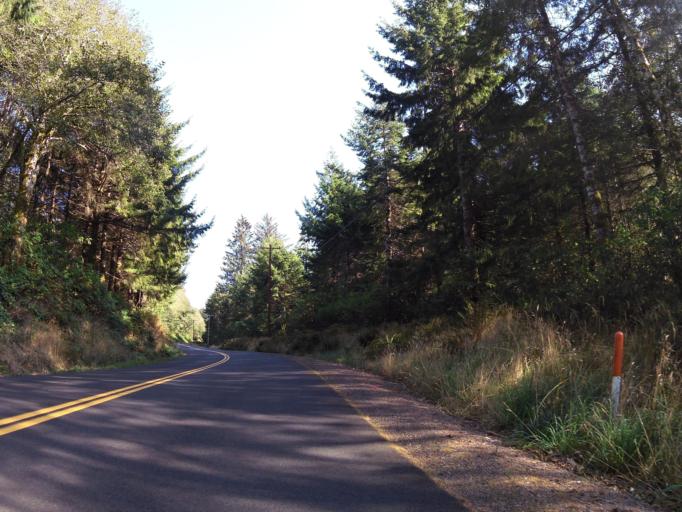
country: US
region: Oregon
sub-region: Lincoln County
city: Rose Lodge
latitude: 45.0852
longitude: -123.9543
